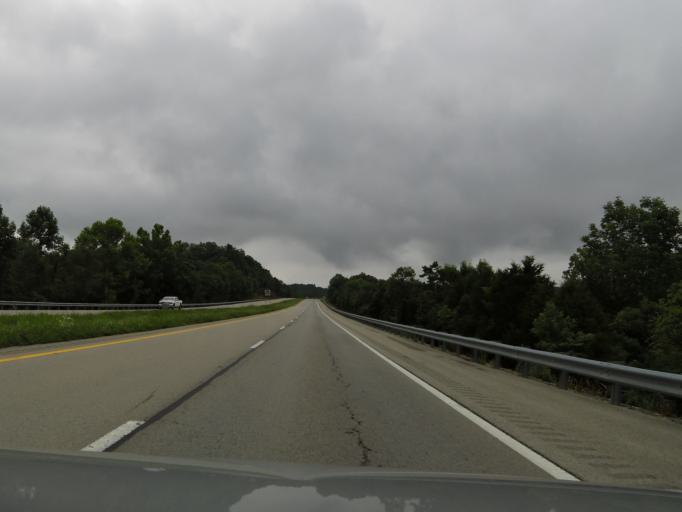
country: US
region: Kentucky
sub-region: Ohio County
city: Oak Grove
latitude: 37.4010
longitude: -86.5579
